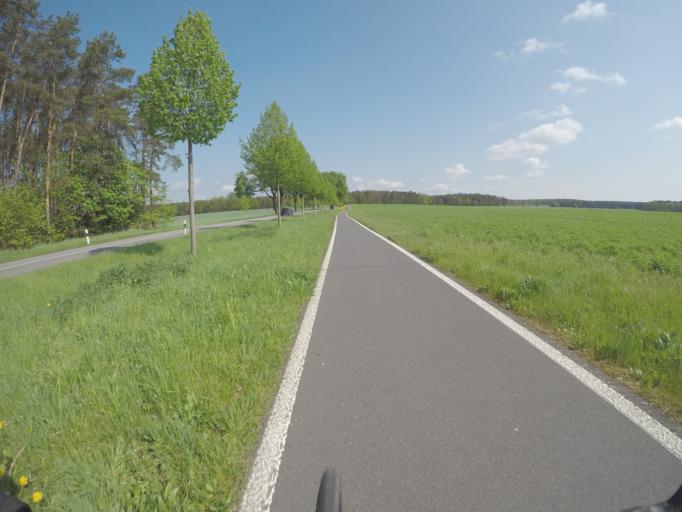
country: DE
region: Brandenburg
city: Wandlitz
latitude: 52.7701
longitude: 13.4768
